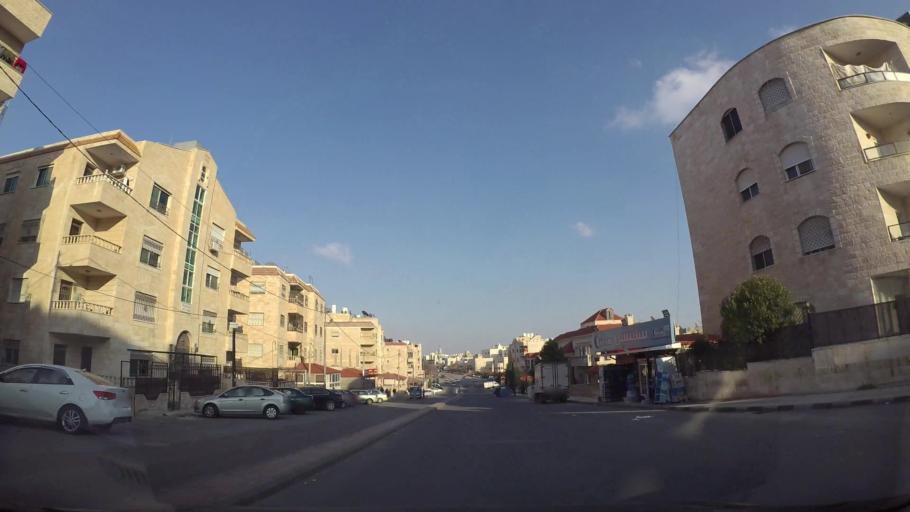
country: JO
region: Amman
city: Amman
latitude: 31.9859
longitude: 35.9441
